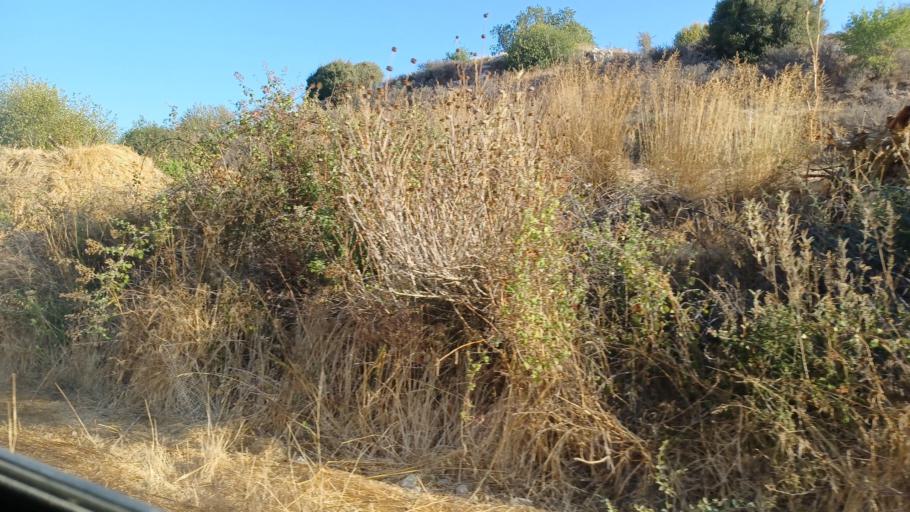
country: CY
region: Pafos
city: Tala
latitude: 34.9243
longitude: 32.4949
